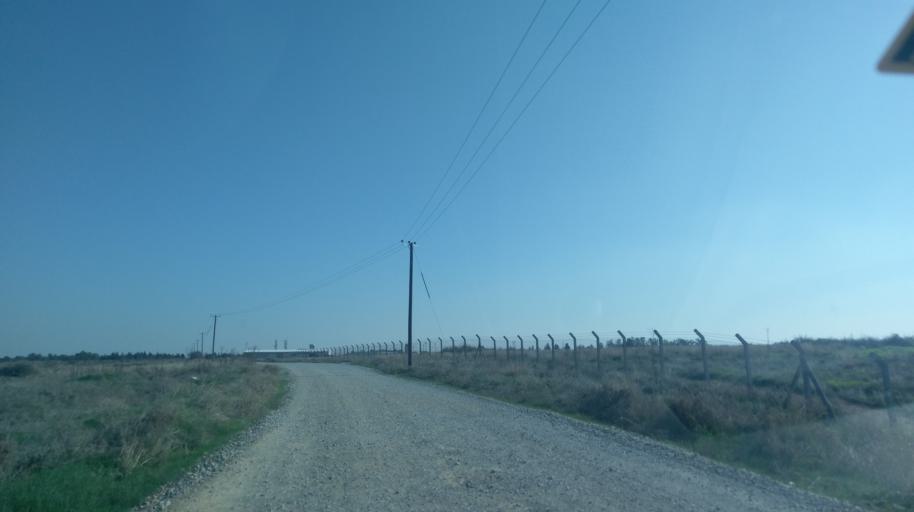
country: CY
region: Lefkosia
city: Geri
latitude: 35.1620
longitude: 33.4939
